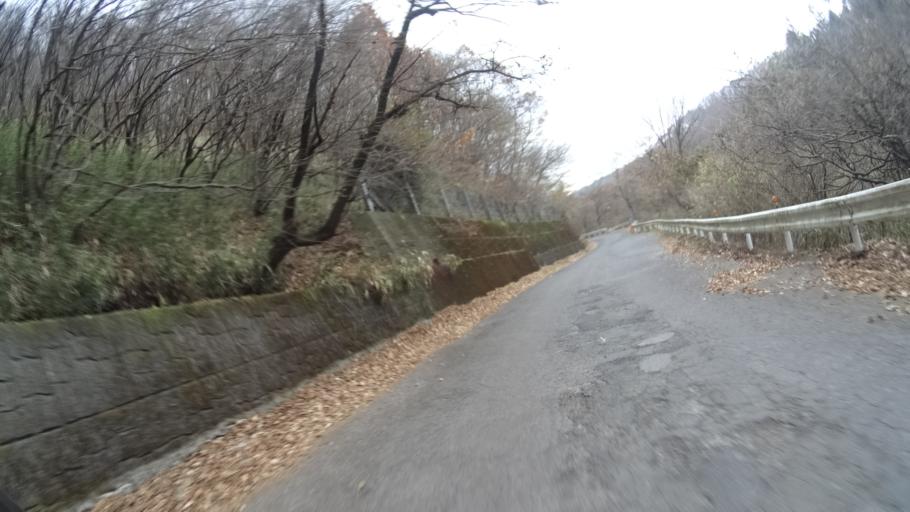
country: JP
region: Gunma
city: Omamacho-omama
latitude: 36.4978
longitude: 139.1833
